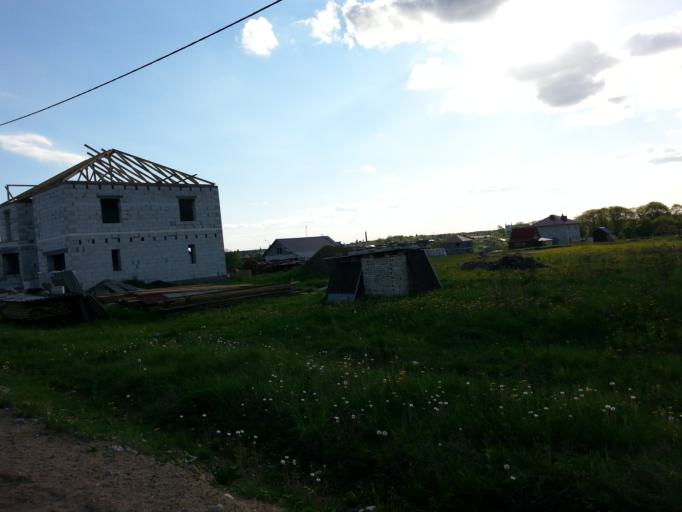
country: BY
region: Minsk
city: Narach
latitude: 54.9381
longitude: 26.6991
